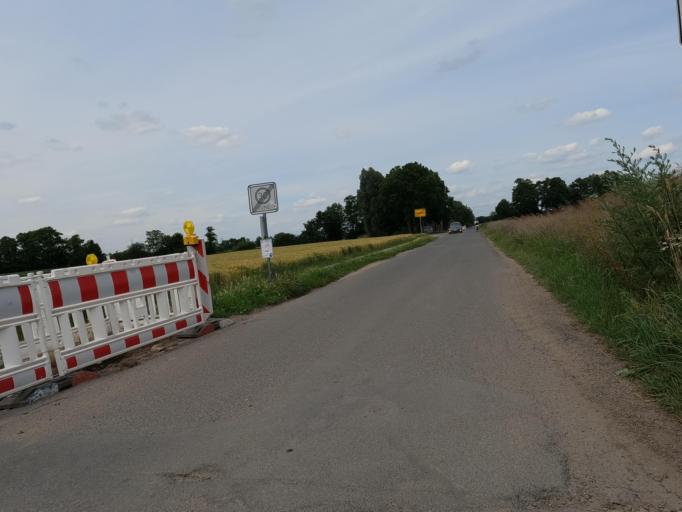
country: DE
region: Hesse
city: Weiterstadt
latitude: 49.9326
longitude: 8.6020
